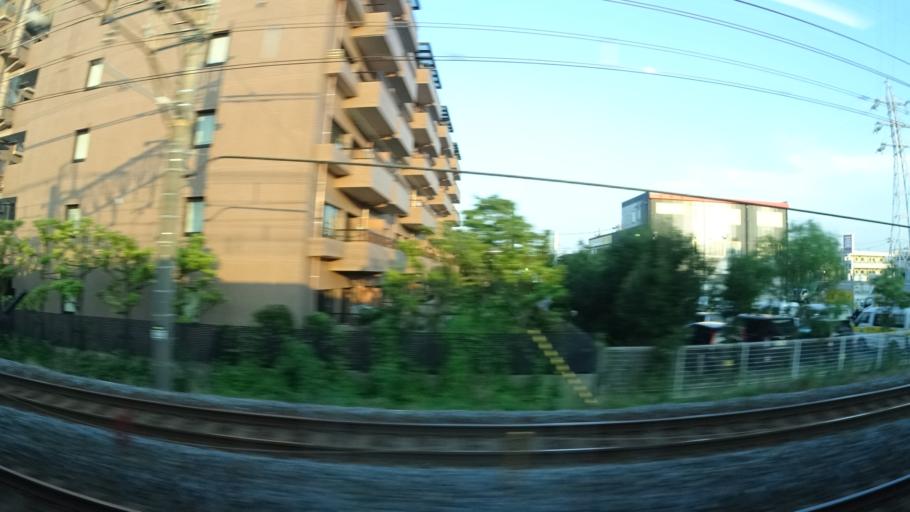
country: JP
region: Chiba
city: Kashiwa
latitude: 35.8489
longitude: 139.9601
